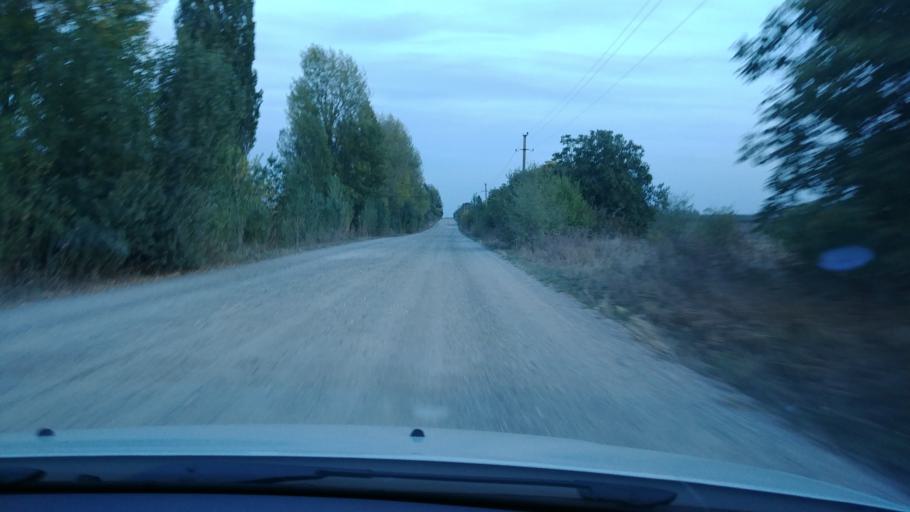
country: MD
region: Rezina
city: Saharna
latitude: 47.6726
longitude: 28.9378
